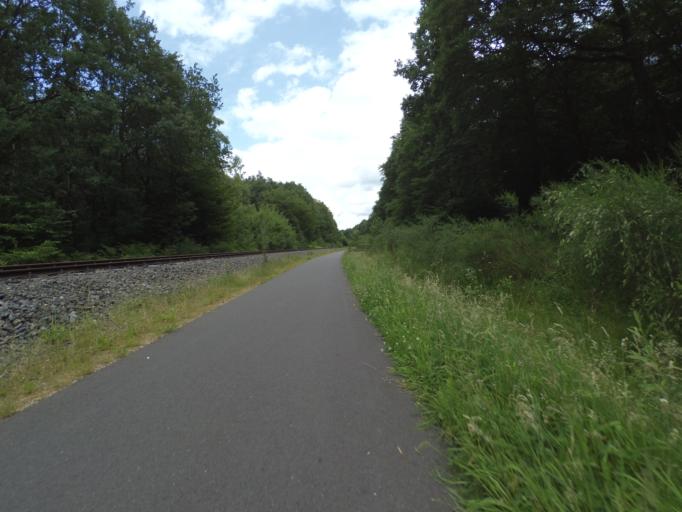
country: BE
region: Wallonia
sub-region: Province de Liege
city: Raeren
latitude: 50.6783
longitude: 6.1546
